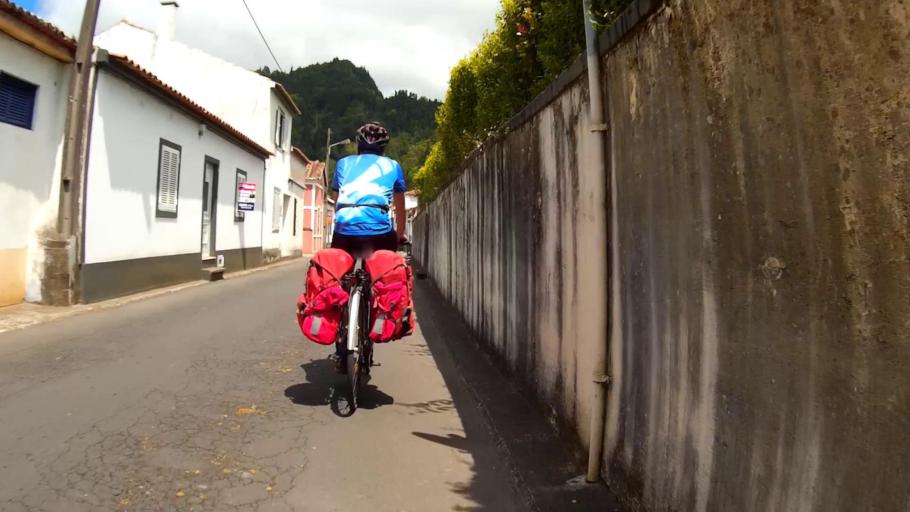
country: PT
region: Azores
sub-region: Povoacao
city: Furnas
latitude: 37.7746
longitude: -25.3117
